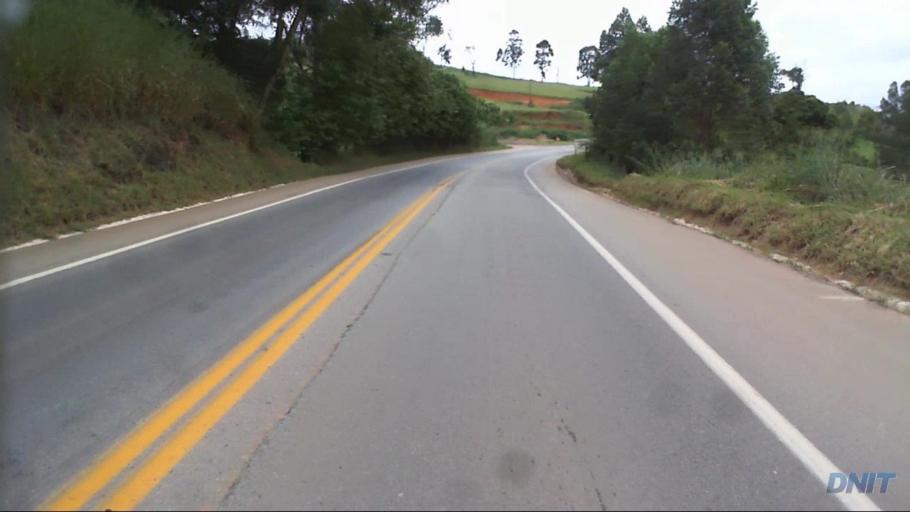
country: BR
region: Minas Gerais
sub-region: Joao Monlevade
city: Joao Monlevade
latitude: -19.8488
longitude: -43.2069
